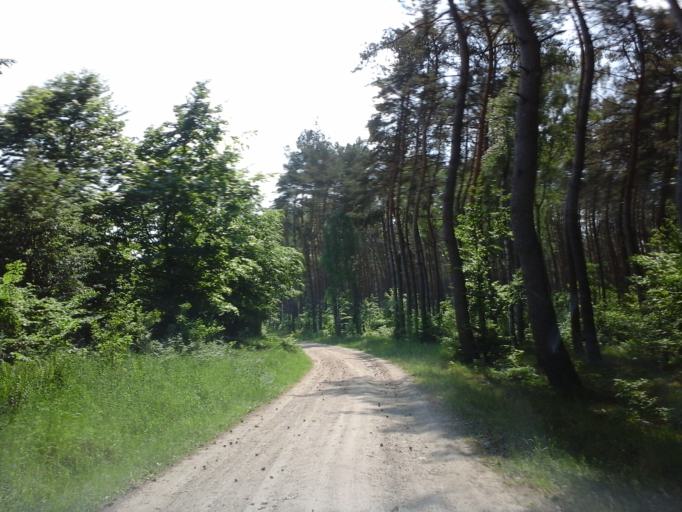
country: PL
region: West Pomeranian Voivodeship
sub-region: Powiat choszczenski
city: Drawno
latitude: 53.2277
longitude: 15.6745
